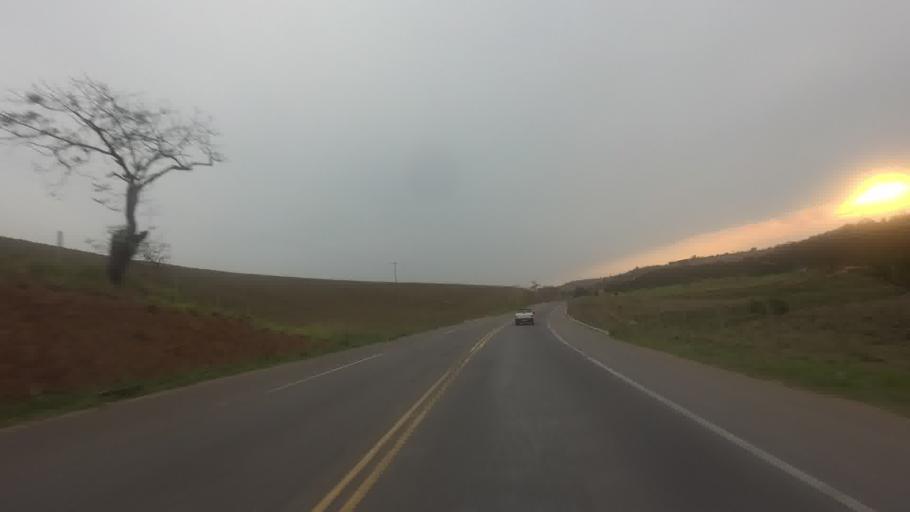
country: BR
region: Minas Gerais
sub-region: Recreio
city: Recreio
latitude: -21.6586
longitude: -42.3718
